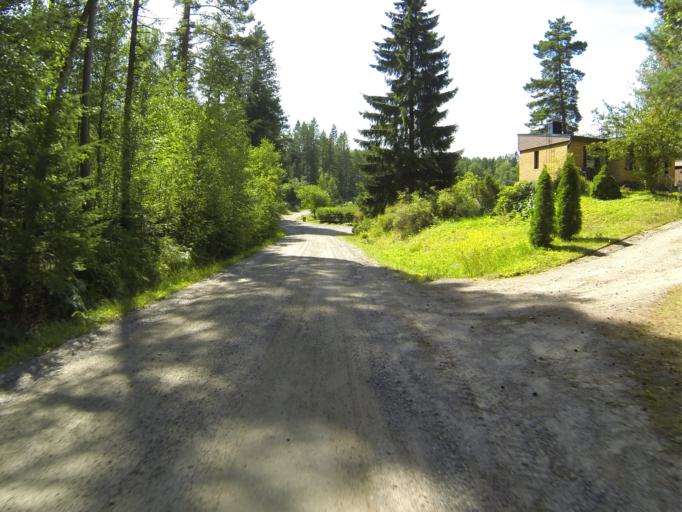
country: FI
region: Varsinais-Suomi
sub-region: Salo
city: Saerkisalo
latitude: 60.2603
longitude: 22.9728
